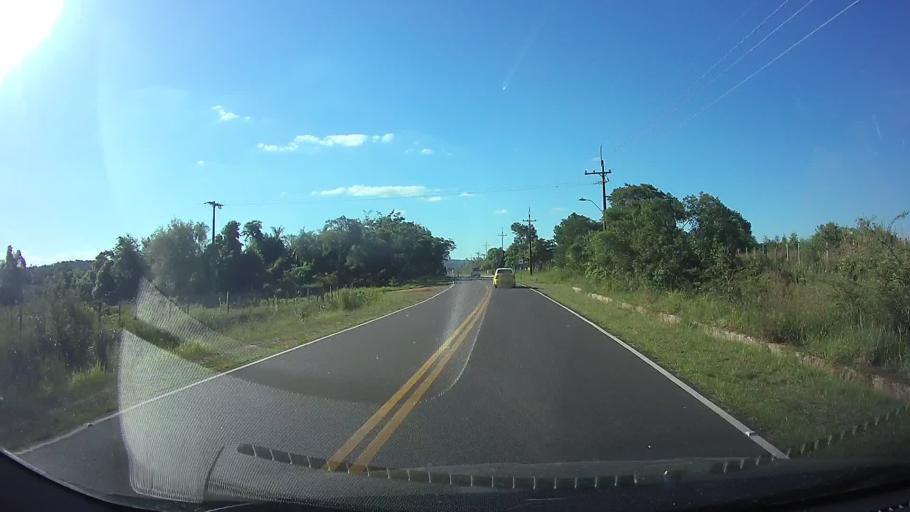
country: PY
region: Cordillera
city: Atyra
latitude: -25.2958
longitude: -57.1633
